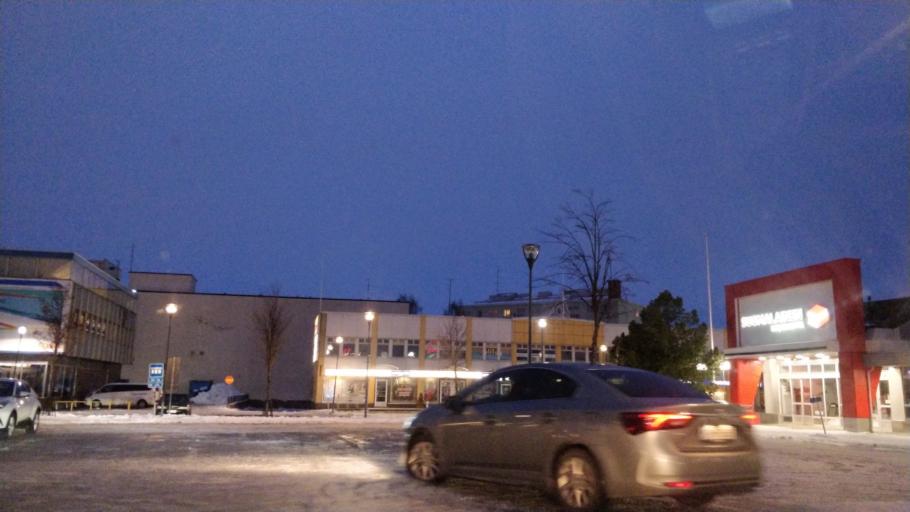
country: FI
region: Lapland
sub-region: Kemi-Tornio
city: Kemi
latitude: 65.7386
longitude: 24.5640
